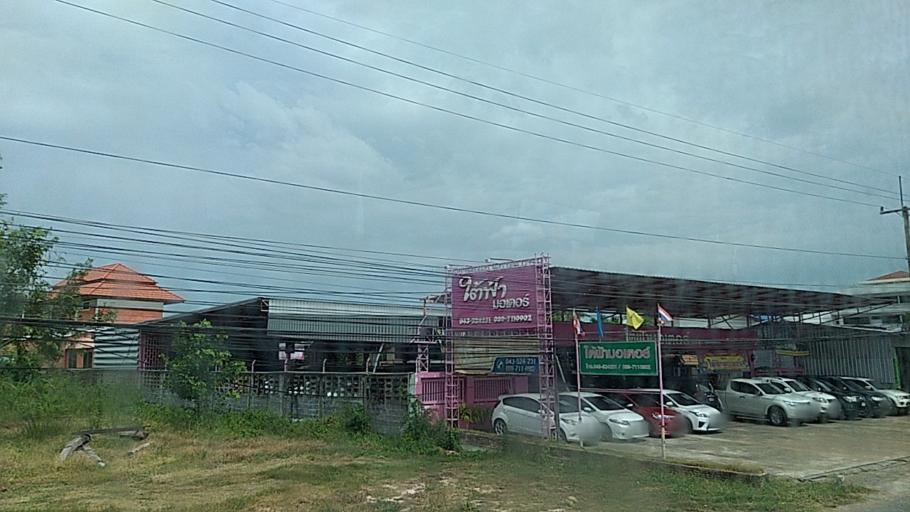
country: TH
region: Roi Et
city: Roi Et
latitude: 16.0679
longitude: 103.6081
